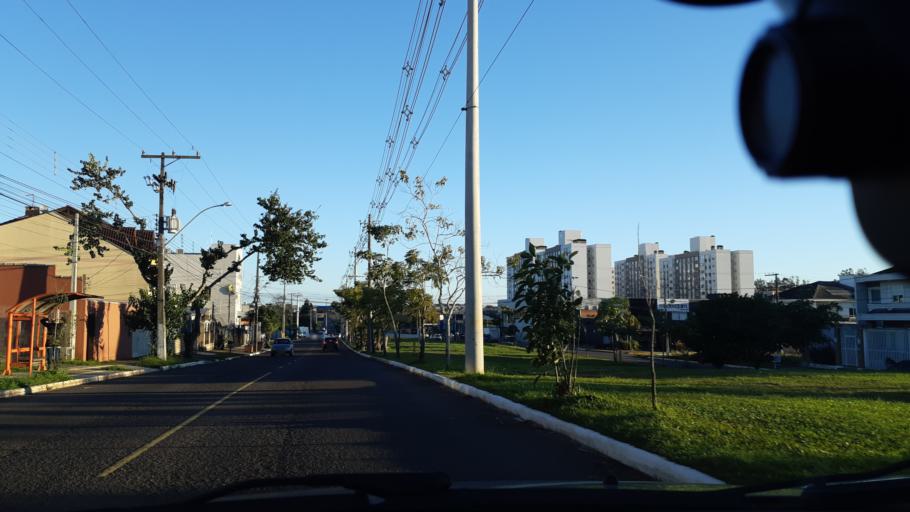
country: BR
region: Rio Grande do Sul
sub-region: Canoas
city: Canoas
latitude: -29.9163
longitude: -51.1545
